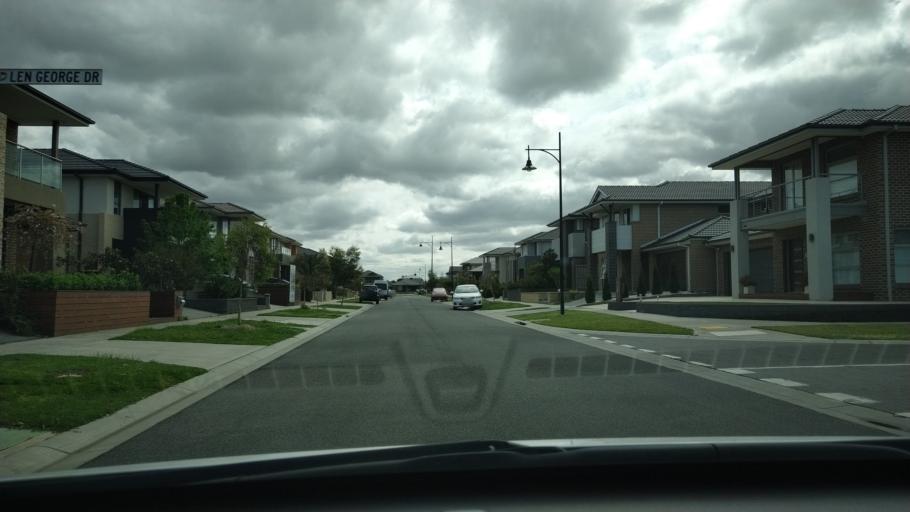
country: AU
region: Victoria
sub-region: Kingston
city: Dingley Village
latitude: -37.9985
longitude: 145.1483
